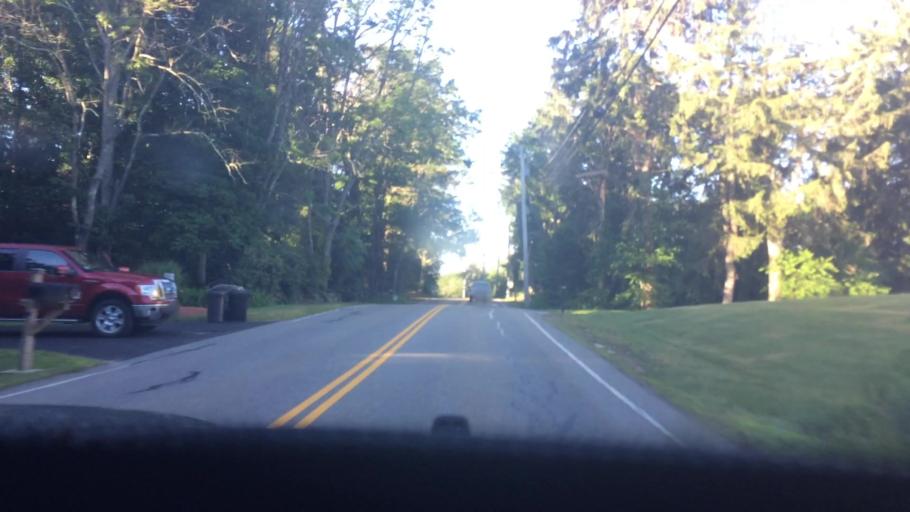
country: US
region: Massachusetts
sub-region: Essex County
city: Andover
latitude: 42.6357
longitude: -71.0899
